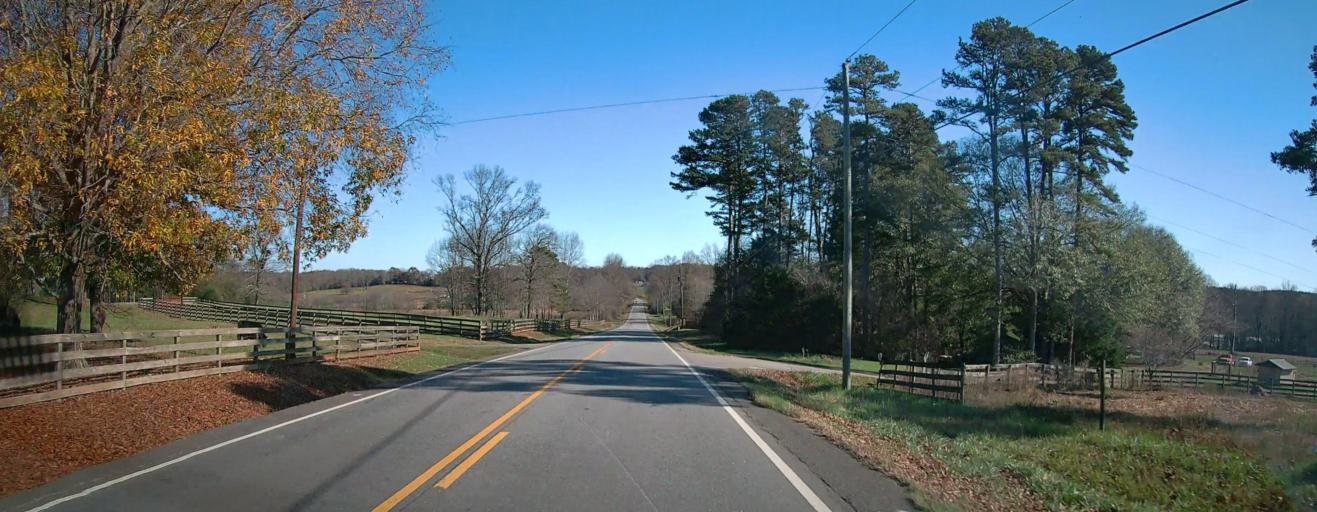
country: US
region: Georgia
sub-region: White County
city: Cleveland
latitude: 34.4766
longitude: -83.7515
